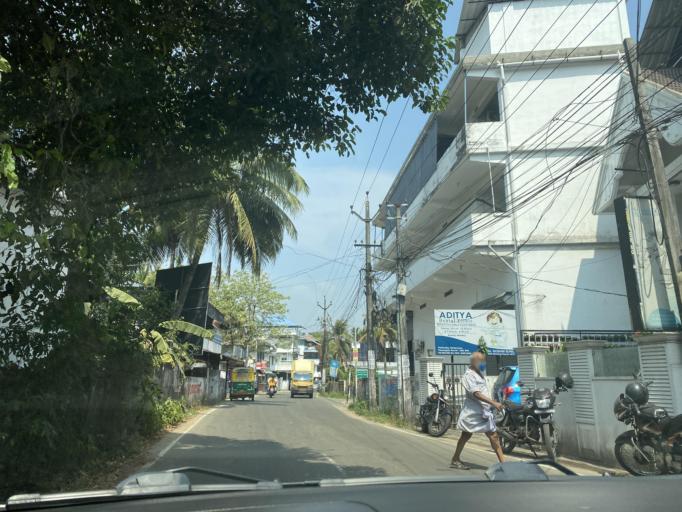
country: IN
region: Kerala
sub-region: Alappuzha
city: Arukutti
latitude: 9.9064
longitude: 76.3198
